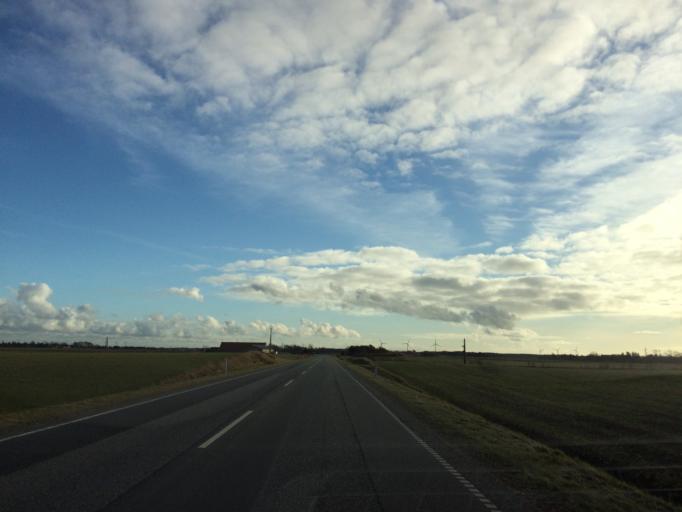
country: DK
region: Central Jutland
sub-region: Lemvig Kommune
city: Lemvig
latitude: 56.4390
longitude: 8.2967
